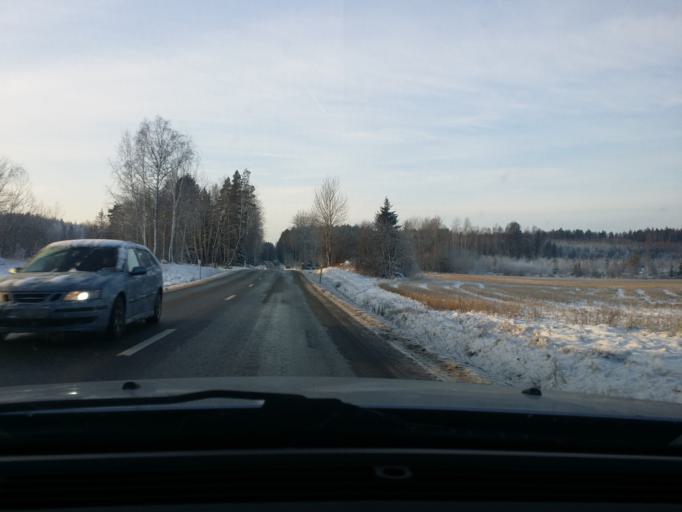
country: SE
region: OErebro
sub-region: Lindesbergs Kommun
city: Fellingsbro
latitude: 59.4651
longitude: 15.5143
